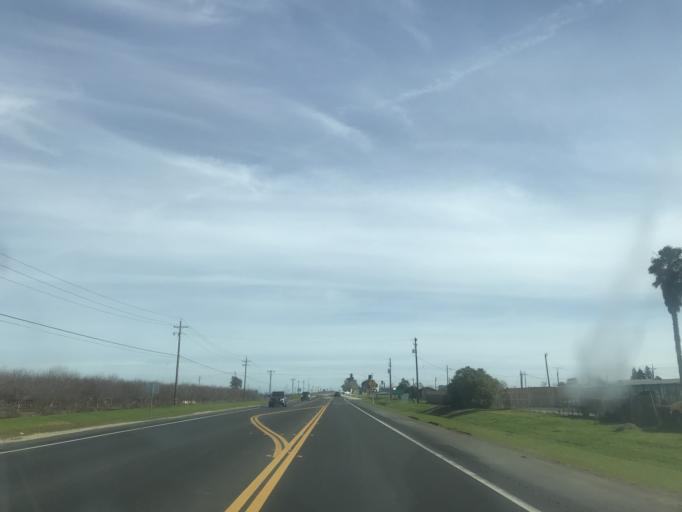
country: US
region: California
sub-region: Yolo County
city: Cottonwood
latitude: 38.6824
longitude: -121.9714
